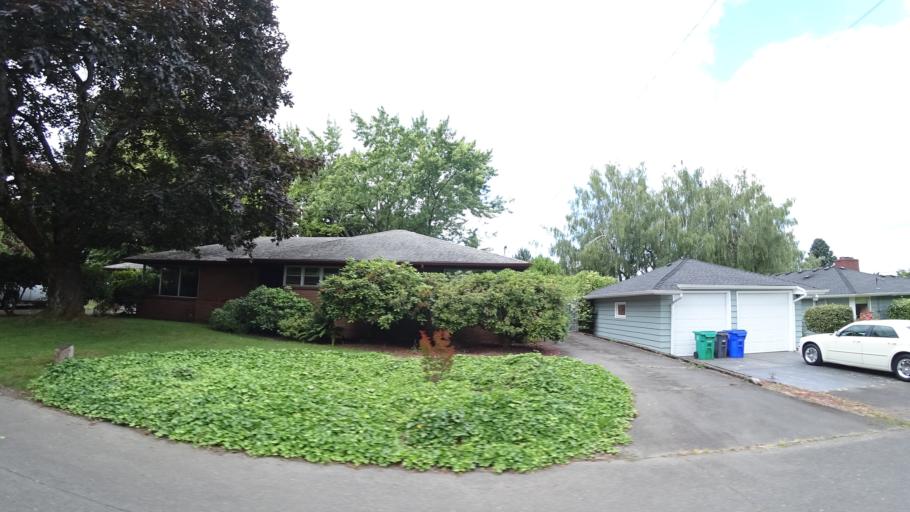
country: US
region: Oregon
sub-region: Multnomah County
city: Portland
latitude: 45.5659
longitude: -122.6092
